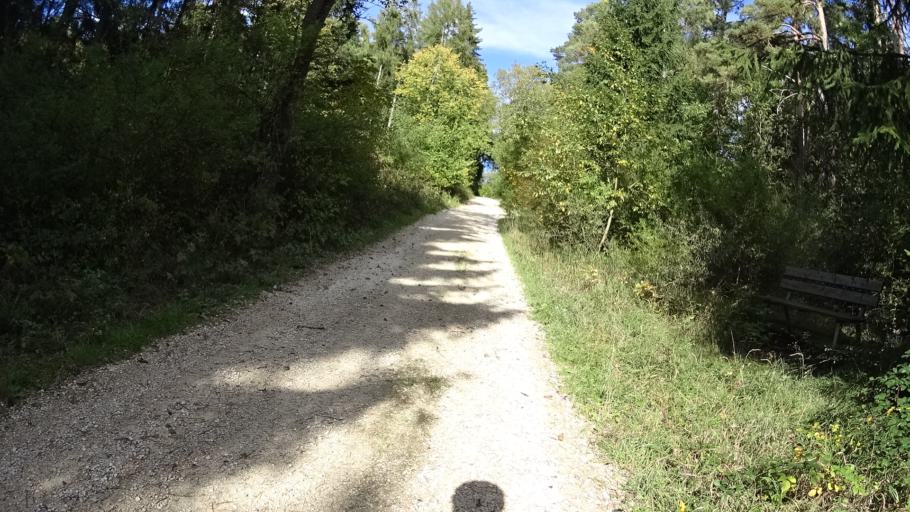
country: DE
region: Bavaria
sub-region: Upper Bavaria
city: Bohmfeld
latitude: 48.8455
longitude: 11.3702
